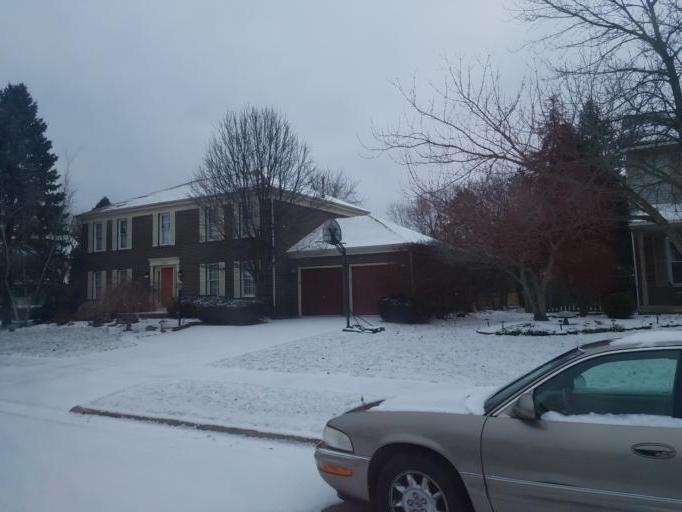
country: US
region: Ohio
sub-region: Delaware County
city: Powell
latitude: 40.1220
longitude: -83.0712
